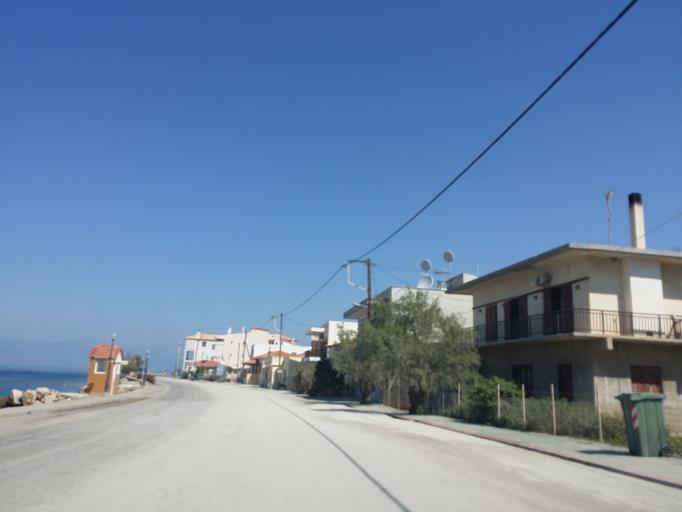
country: GR
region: West Greece
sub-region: Nomos Achaias
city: Aiyira
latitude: 38.1299
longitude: 22.4509
